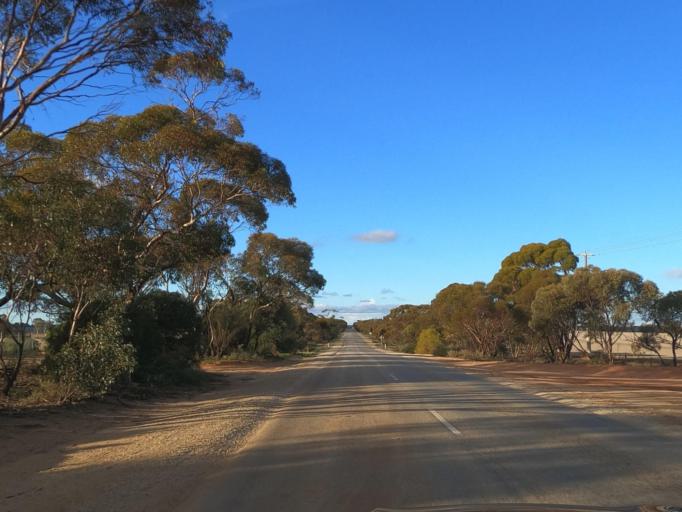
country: AU
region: Victoria
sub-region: Swan Hill
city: Swan Hill
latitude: -35.3488
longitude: 143.5143
